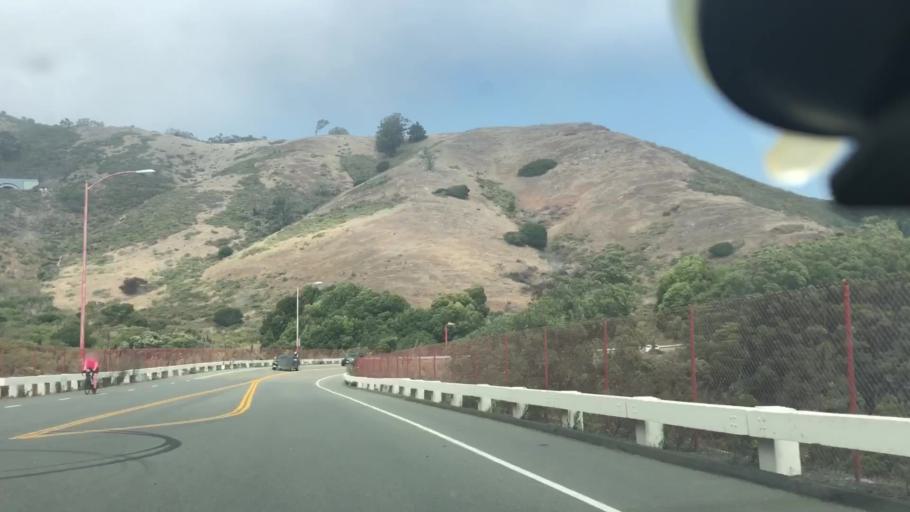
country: US
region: California
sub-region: Marin County
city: Sausalito
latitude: 37.8378
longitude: -122.4830
